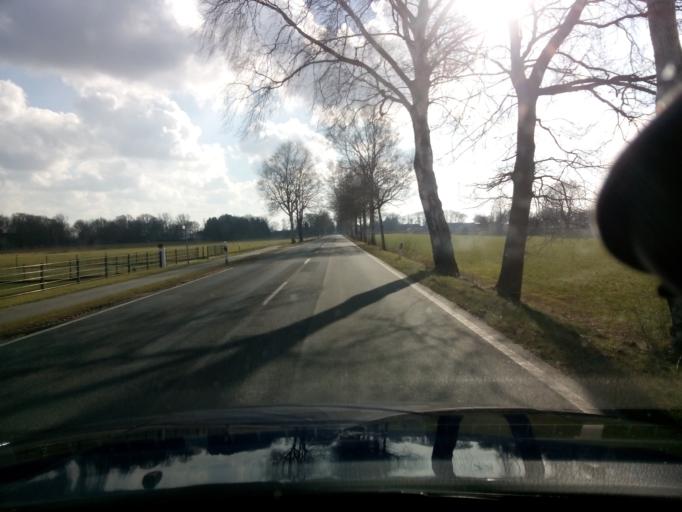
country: DE
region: Lower Saxony
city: Vollersode
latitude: 53.3201
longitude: 8.9784
